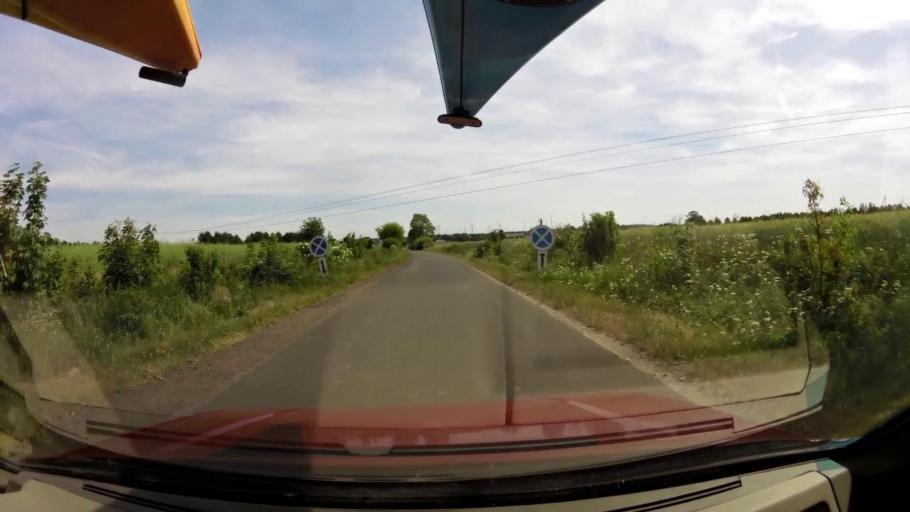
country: PL
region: West Pomeranian Voivodeship
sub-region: Powiat slawienski
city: Darlowo
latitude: 54.3052
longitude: 16.4969
